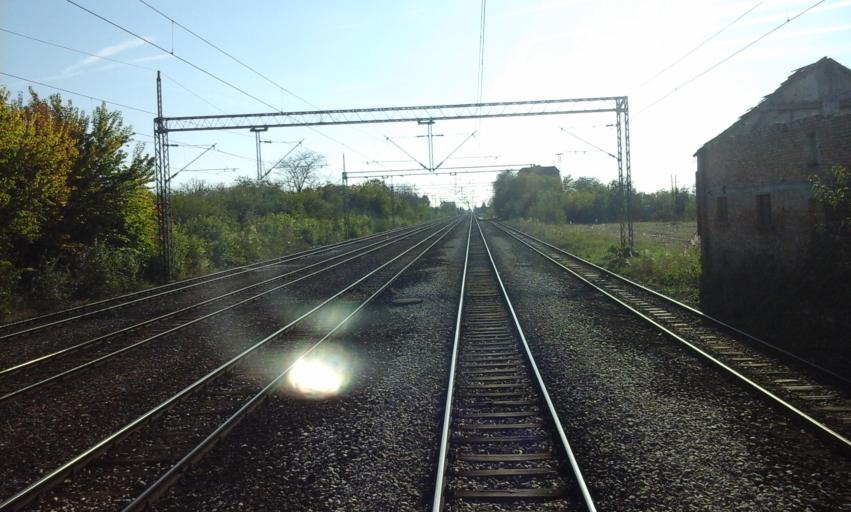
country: RS
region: Autonomna Pokrajina Vojvodina
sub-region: Severnobacki Okrug
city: Subotica
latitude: 46.0260
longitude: 19.6816
